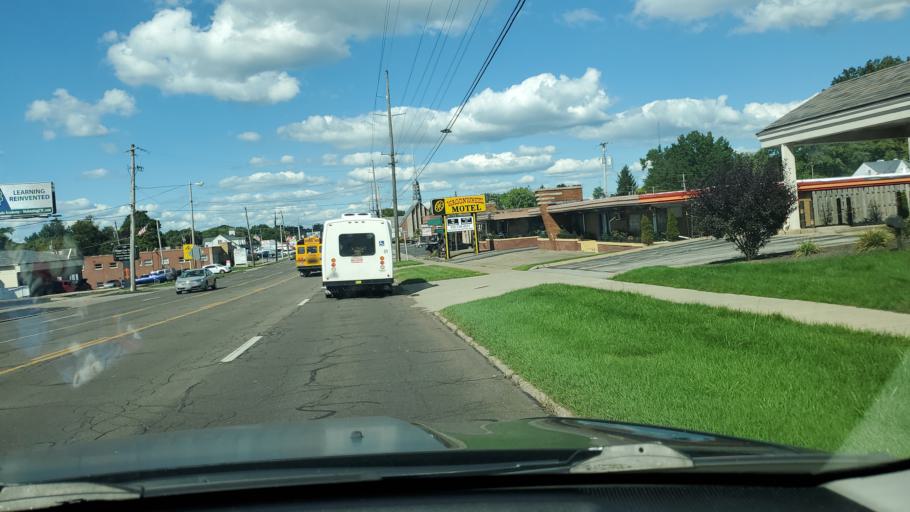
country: US
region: Ohio
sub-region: Mahoning County
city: Boardman
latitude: 41.0267
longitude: -80.6627
